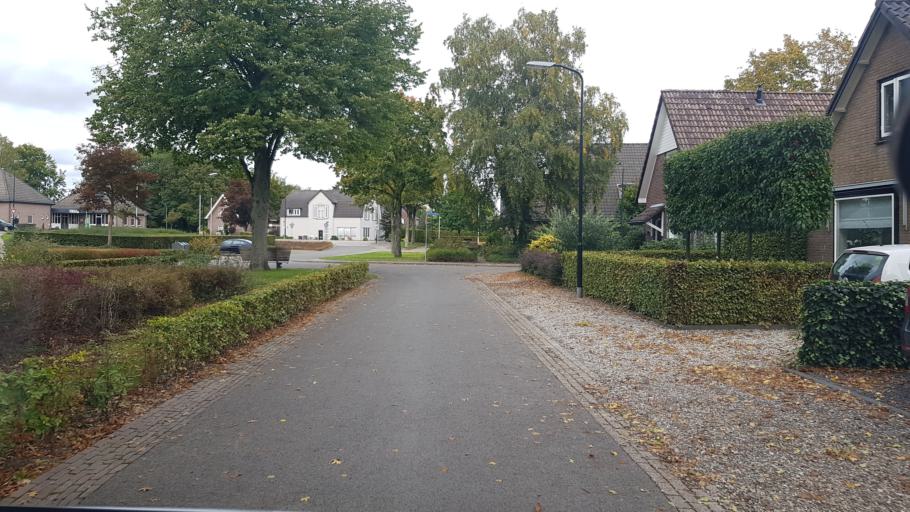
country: NL
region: Gelderland
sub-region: Gemeente Apeldoorn
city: Loenen
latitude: 52.1167
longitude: 6.0203
